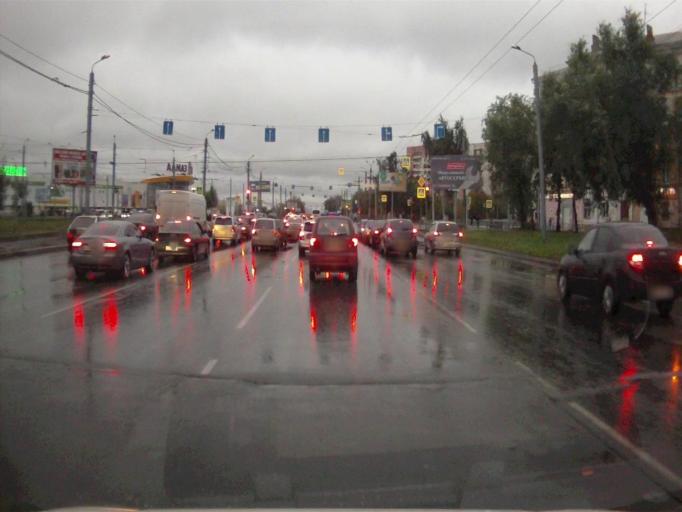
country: RU
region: Chelyabinsk
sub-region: Gorod Chelyabinsk
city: Chelyabinsk
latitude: 55.1474
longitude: 61.4446
